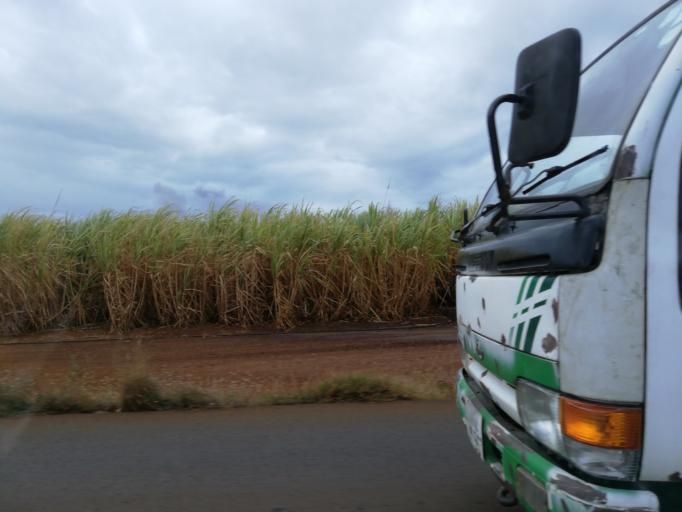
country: MU
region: Black River
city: Petite Riviere
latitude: -20.2129
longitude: 57.4553
